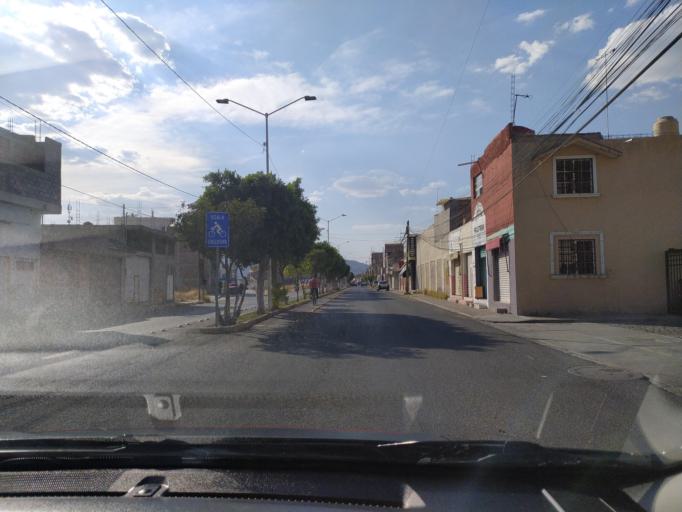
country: MX
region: Guanajuato
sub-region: San Francisco del Rincon
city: Fraccionamiento la Mezquitera
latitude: 21.0132
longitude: -101.8428
